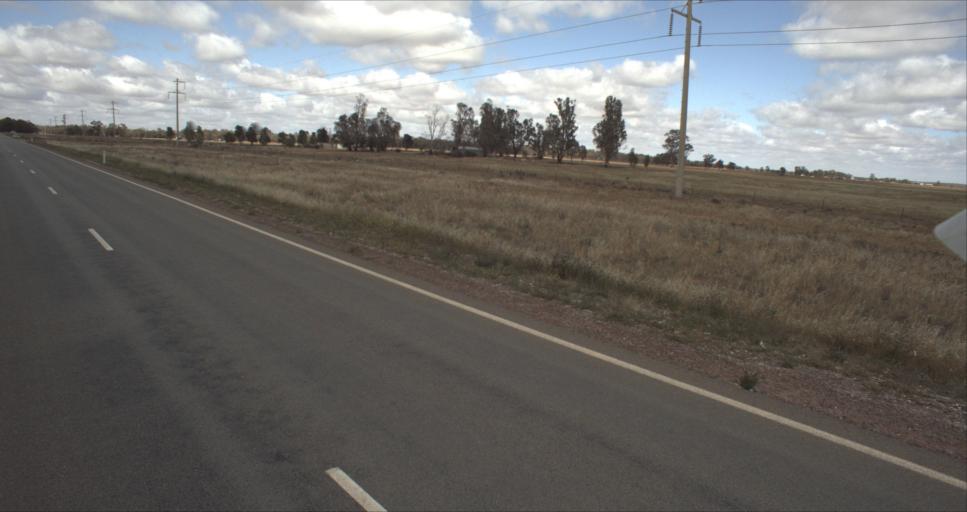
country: AU
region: New South Wales
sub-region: Murrumbidgee Shire
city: Darlington Point
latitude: -34.5906
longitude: 146.1636
